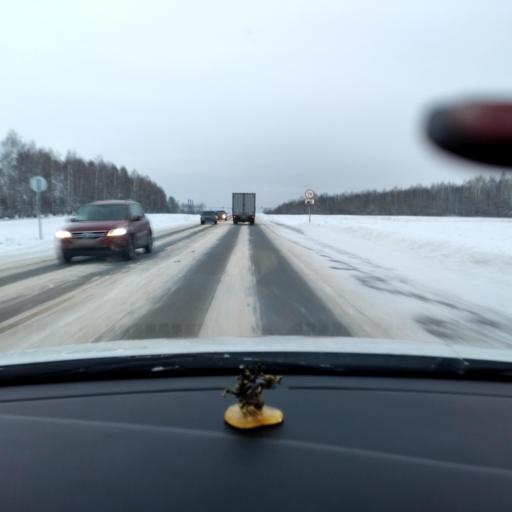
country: RU
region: Tatarstan
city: Vysokaya Gora
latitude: 55.9810
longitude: 49.4752
